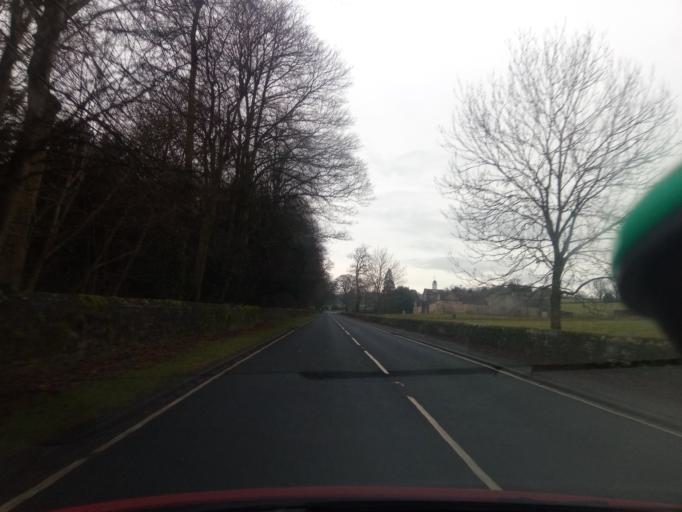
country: GB
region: England
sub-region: Northumberland
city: Wall
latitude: 55.0286
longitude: -2.1416
